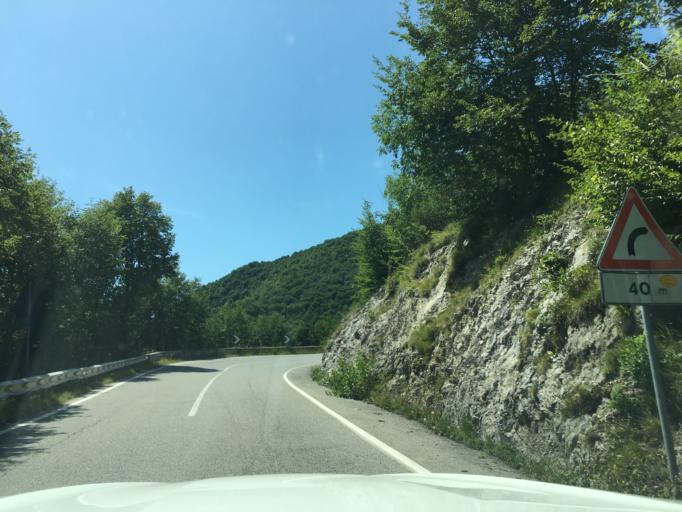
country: IT
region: Lombardy
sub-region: Provincia di Bergamo
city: Selvino
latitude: 45.7702
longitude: 9.7427
